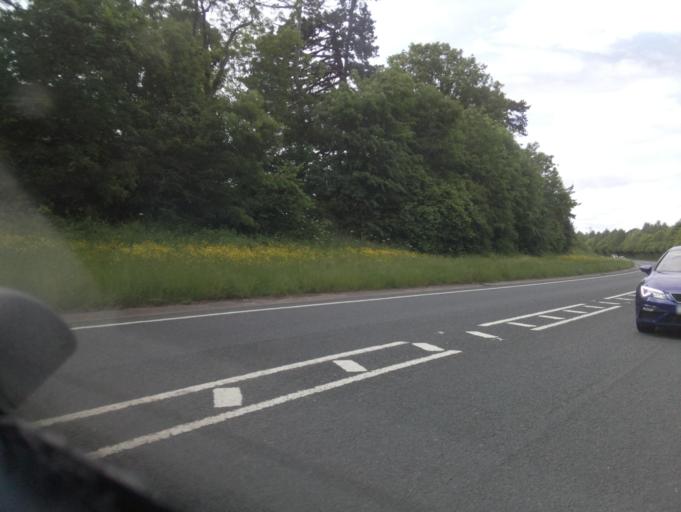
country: GB
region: England
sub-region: Worcestershire
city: Worcester
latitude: 52.1754
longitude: -2.2491
